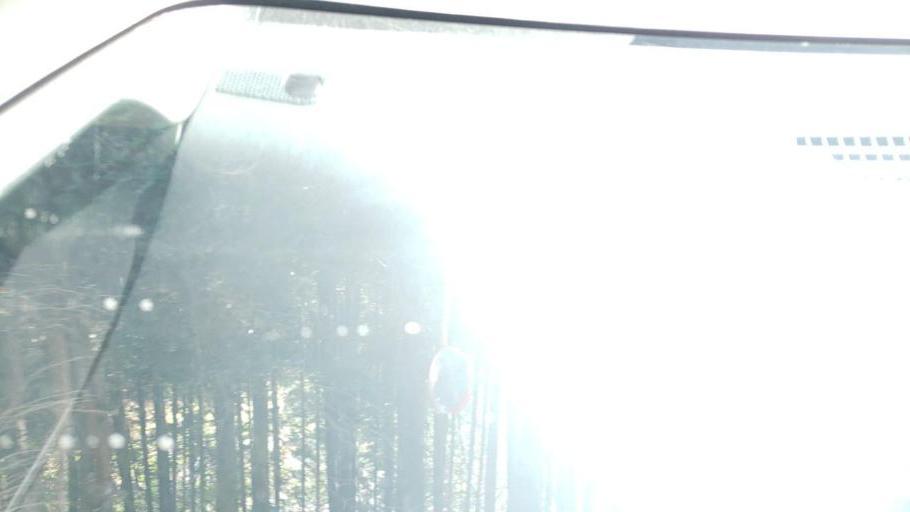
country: JP
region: Tokushima
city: Narutocho-mitsuishi
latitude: 34.1990
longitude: 134.5536
